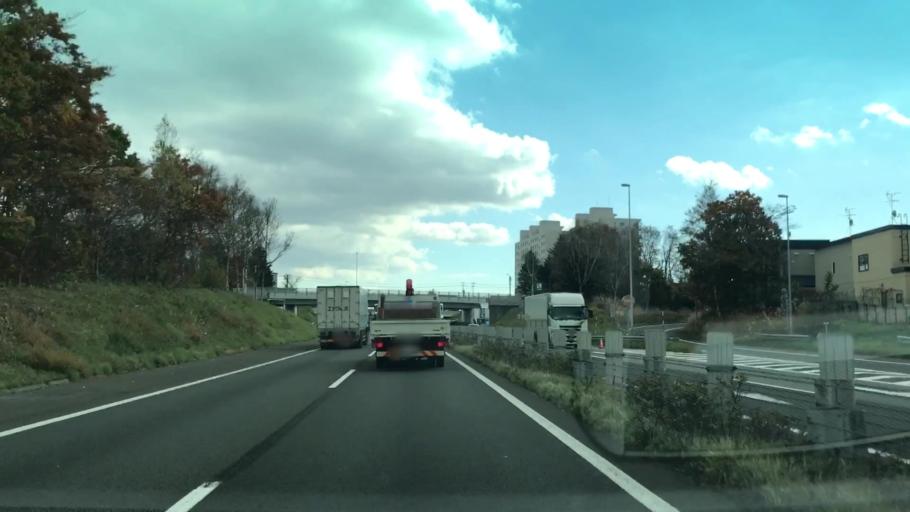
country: JP
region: Hokkaido
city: Kitahiroshima
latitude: 42.9780
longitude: 141.4772
